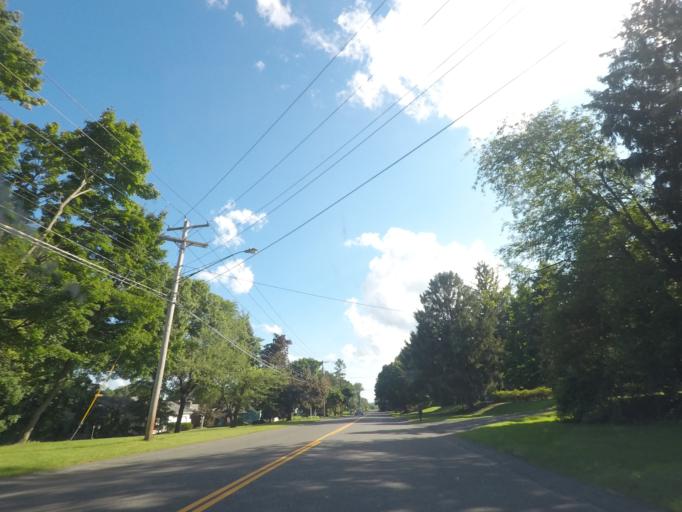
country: US
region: New York
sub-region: Albany County
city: Albany
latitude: 42.6753
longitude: -73.7443
